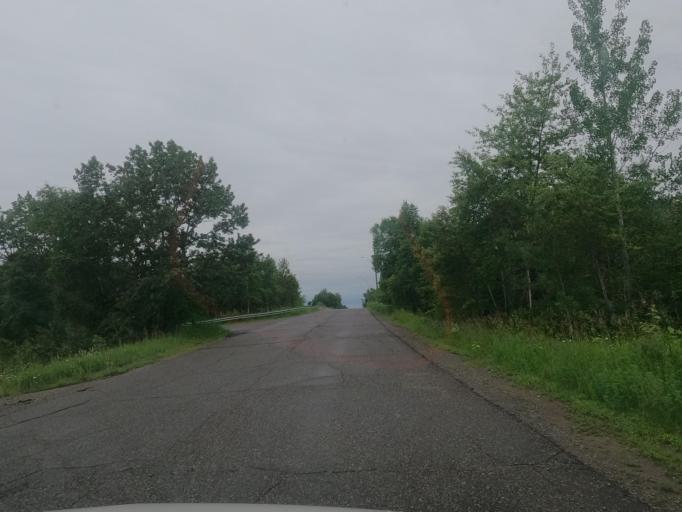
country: CA
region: Ontario
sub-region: Thunder Bay District
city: Thunder Bay
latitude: 48.4537
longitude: -89.1833
